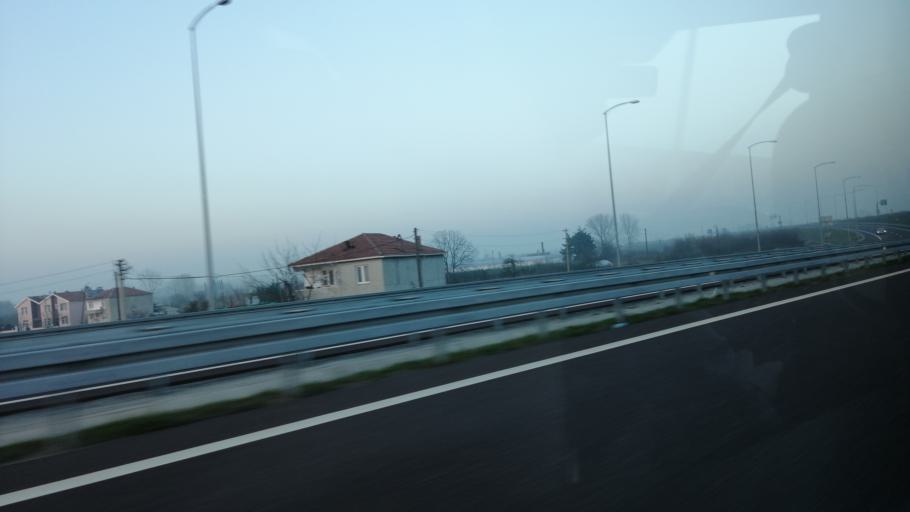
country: TR
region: Yalova
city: Altinova
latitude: 40.6968
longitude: 29.4819
